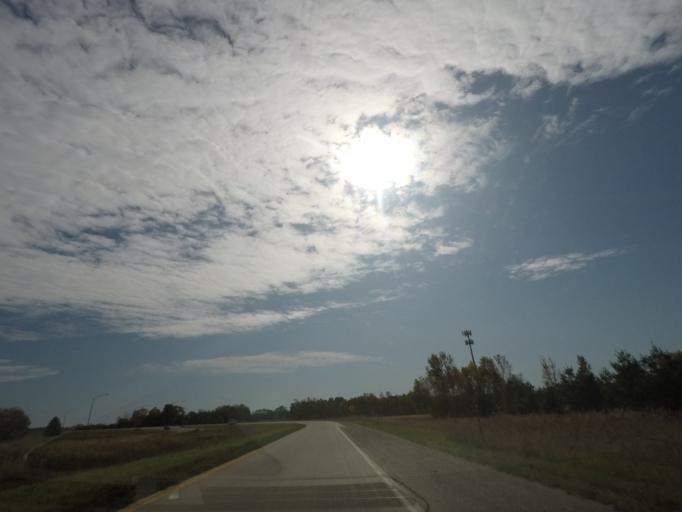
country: US
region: Iowa
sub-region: Story County
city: Ames
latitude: 42.0082
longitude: -93.6823
